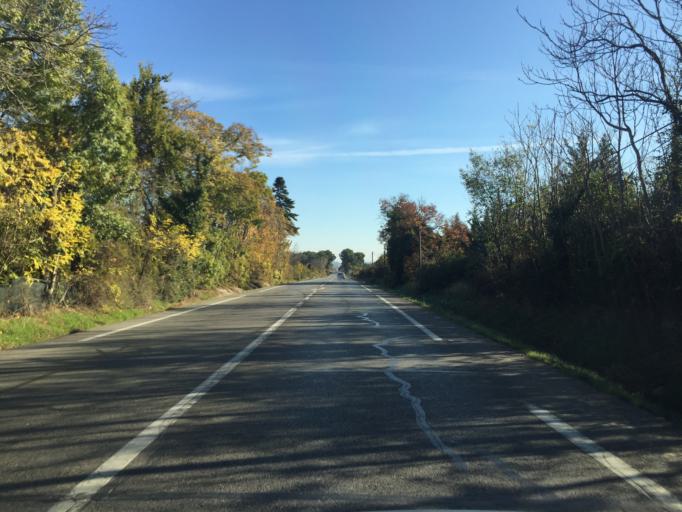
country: FR
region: Provence-Alpes-Cote d'Azur
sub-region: Departement des Bouches-du-Rhone
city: Eguilles
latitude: 43.5978
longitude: 5.3502
